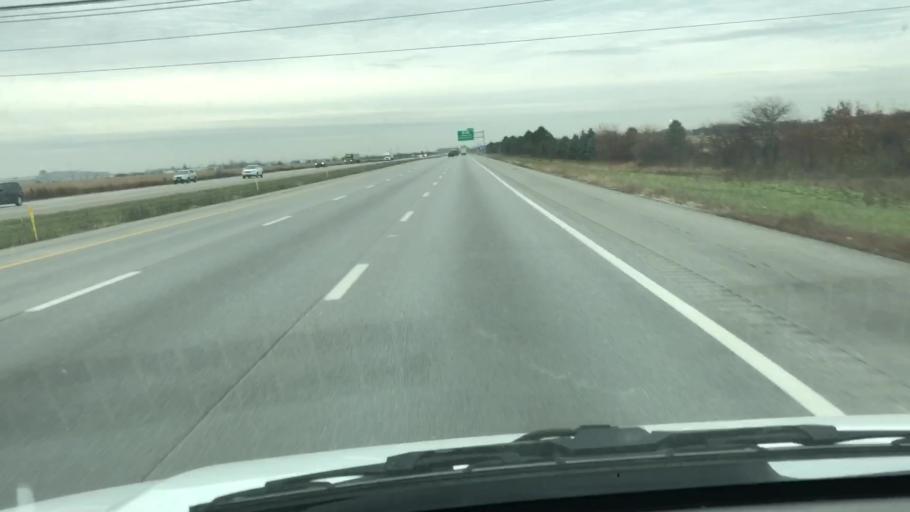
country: US
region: Ohio
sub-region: Wood County
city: Bowling Green
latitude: 41.3999
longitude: -83.6161
